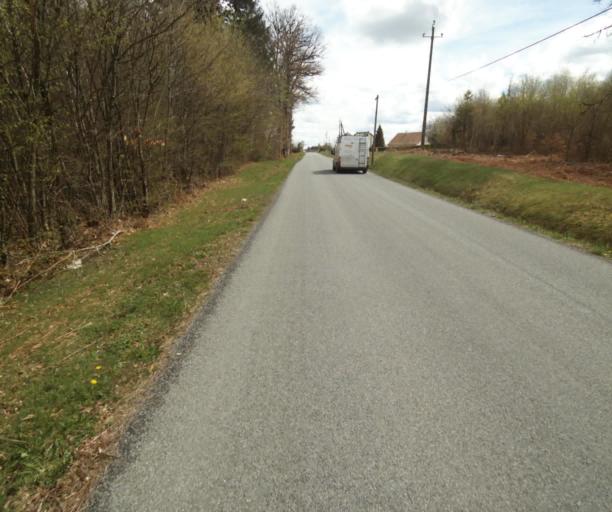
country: FR
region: Limousin
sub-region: Departement de la Correze
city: Laguenne
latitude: 45.2046
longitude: 1.8891
